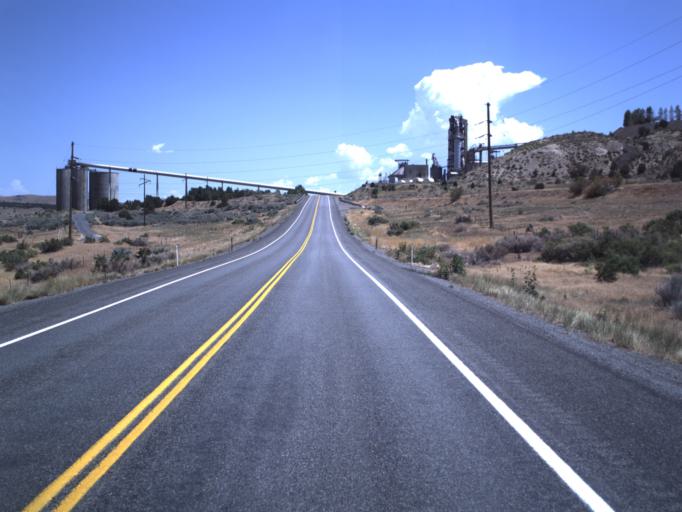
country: US
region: Utah
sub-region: Juab County
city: Nephi
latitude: 39.5595
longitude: -112.2046
